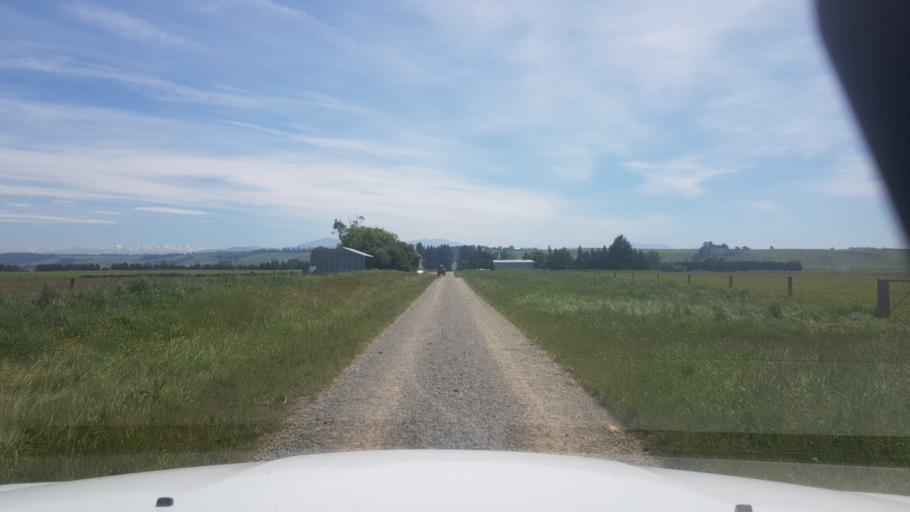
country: NZ
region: Canterbury
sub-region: Timaru District
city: Pleasant Point
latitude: -44.2273
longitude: 171.1651
